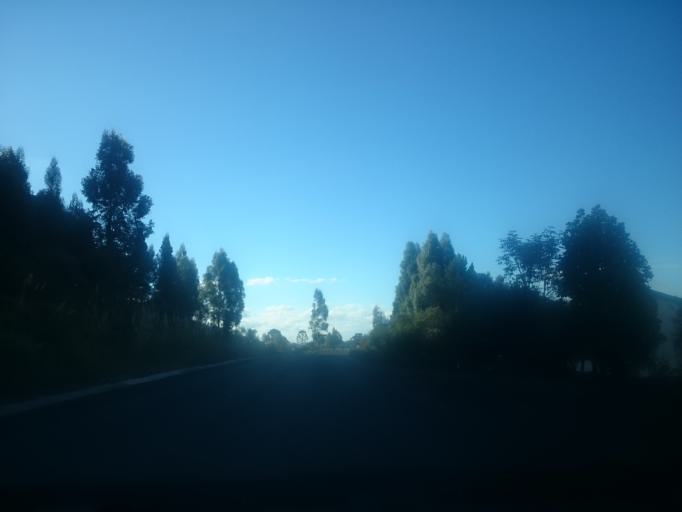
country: BR
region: Santa Catarina
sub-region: Sao Joaquim
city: Sao Joaquim
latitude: -28.1967
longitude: -49.9949
